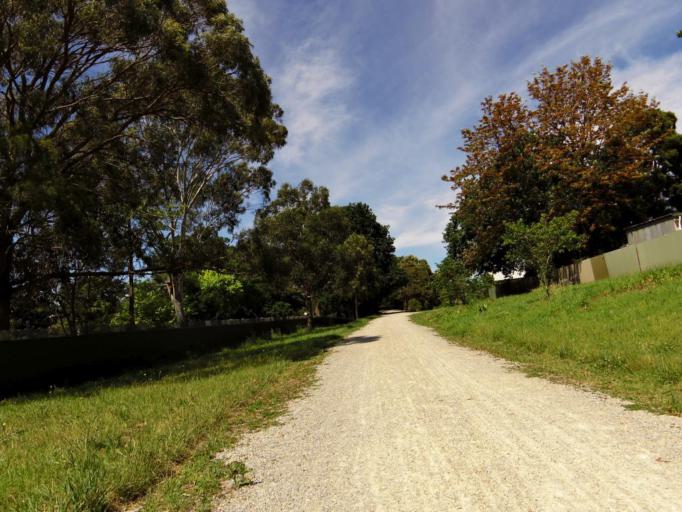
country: AU
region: Victoria
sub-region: Yarra Ranges
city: Lilydale
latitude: -37.7546
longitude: 145.3597
